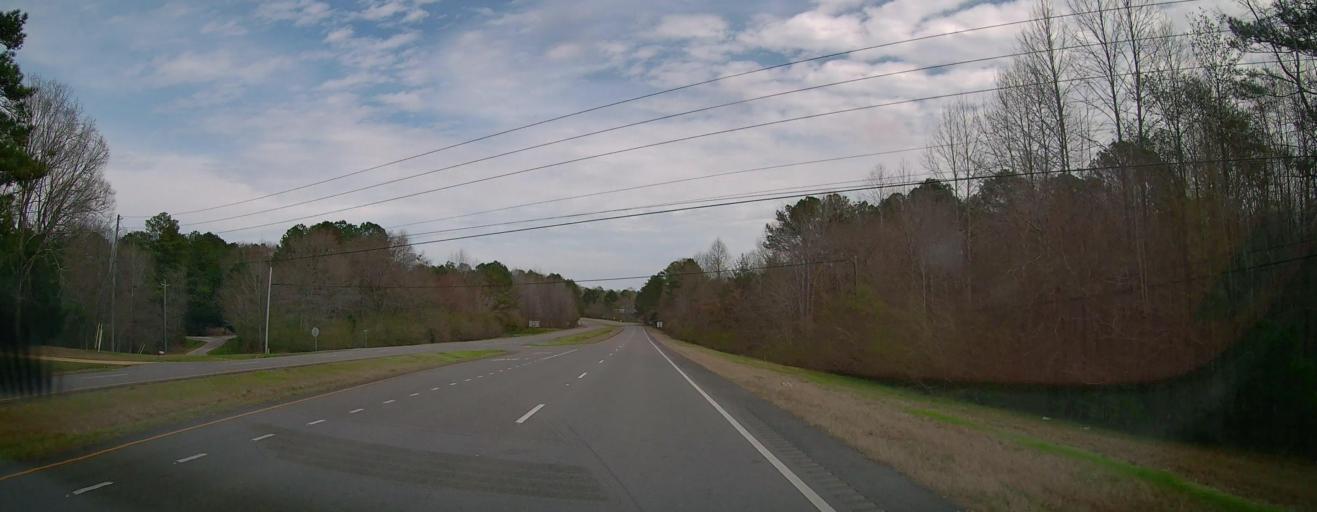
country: US
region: Alabama
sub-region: Marion County
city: Winfield
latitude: 33.9288
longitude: -87.7650
